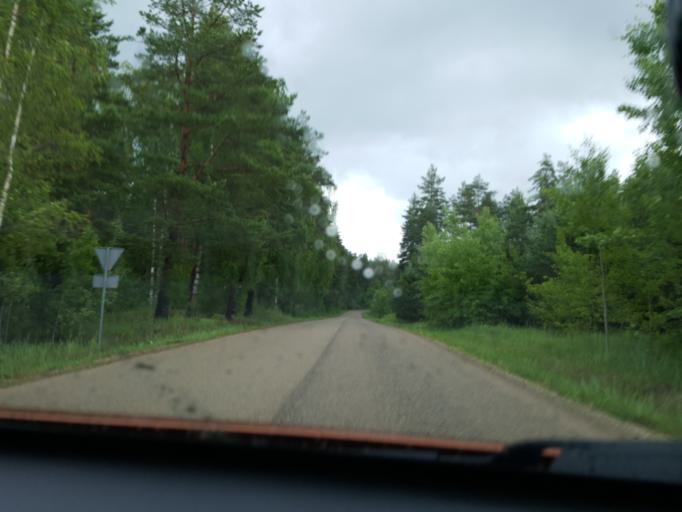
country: LV
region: Ikskile
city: Ikskile
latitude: 56.8865
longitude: 24.4959
